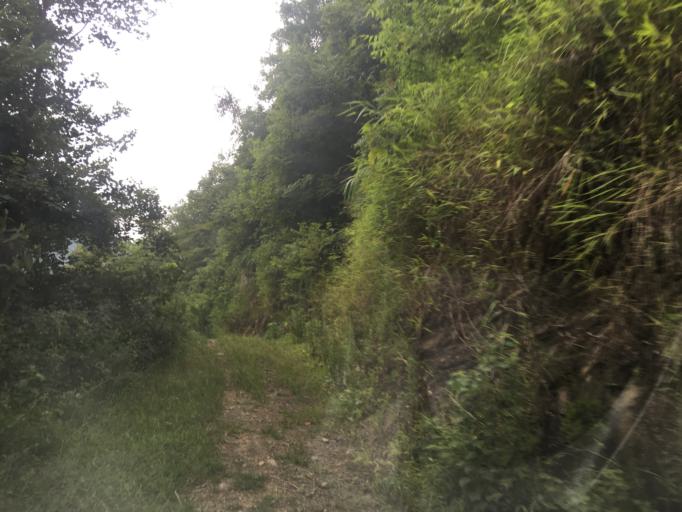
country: CN
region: Guangxi Zhuangzu Zizhiqu
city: Xinzhou
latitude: 25.1664
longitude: 105.6997
